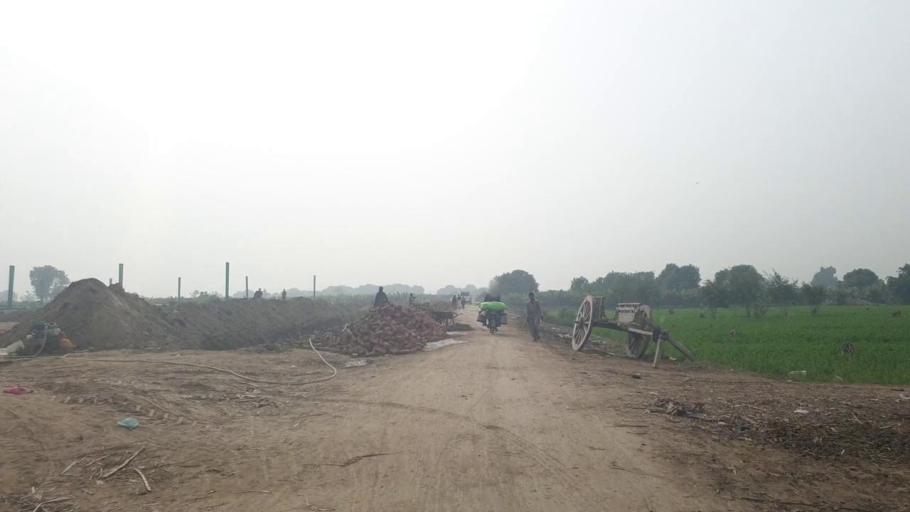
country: PK
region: Sindh
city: Tando Adam
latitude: 25.7158
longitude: 68.6263
